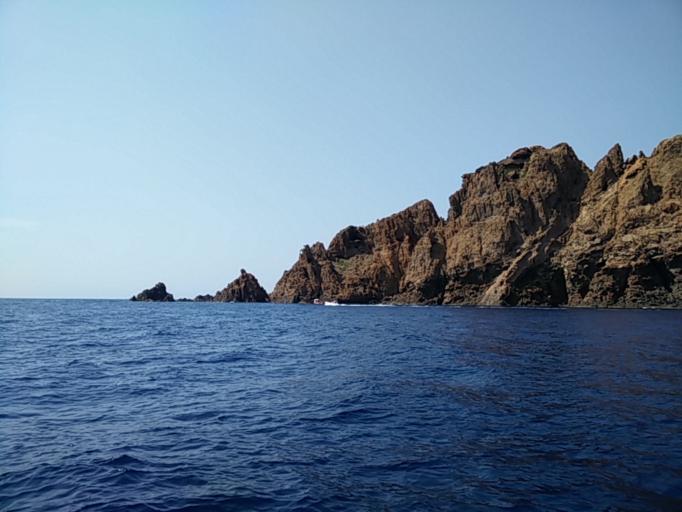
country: FR
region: Corsica
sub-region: Departement de la Corse-du-Sud
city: Cargese
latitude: 42.3314
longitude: 8.5558
